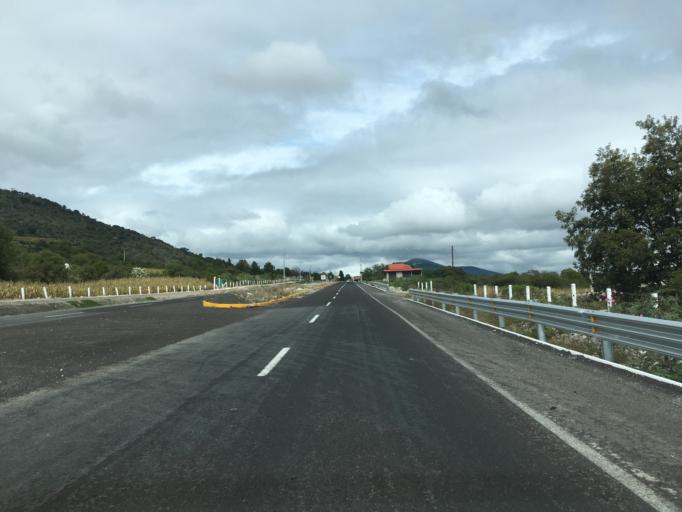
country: MX
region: Hidalgo
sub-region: Atotonilco el Grande
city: Santa Maria Amajac
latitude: 20.3585
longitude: -98.7187
